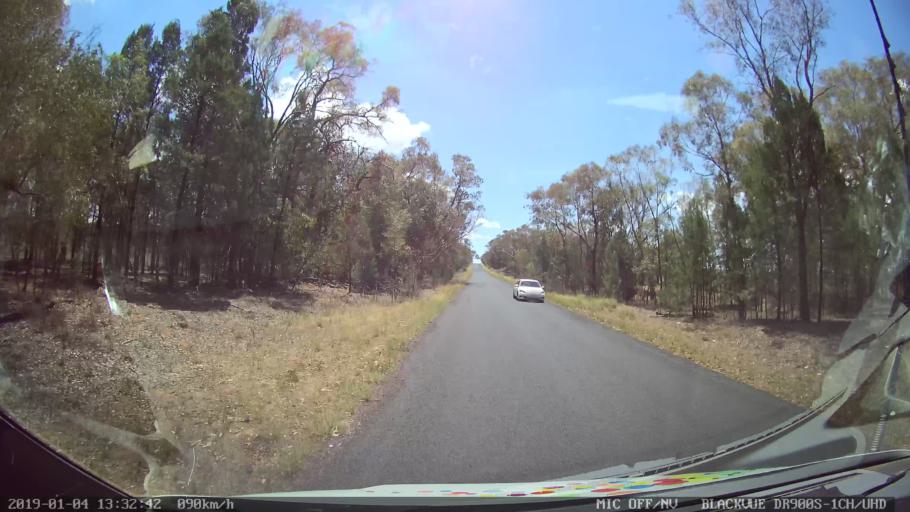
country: AU
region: New South Wales
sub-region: Dubbo Municipality
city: Eulomogo
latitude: -32.6061
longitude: 148.5470
